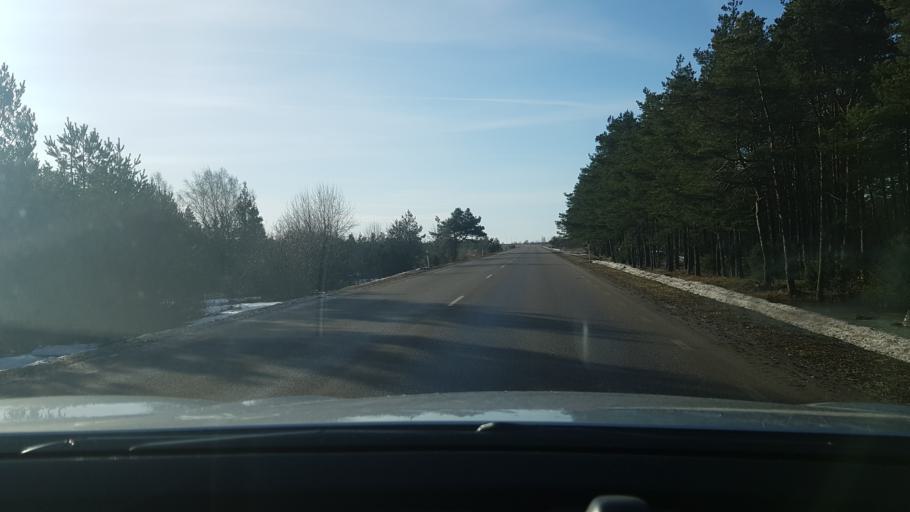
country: EE
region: Saare
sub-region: Kuressaare linn
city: Kuressaare
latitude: 58.2435
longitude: 22.5037
